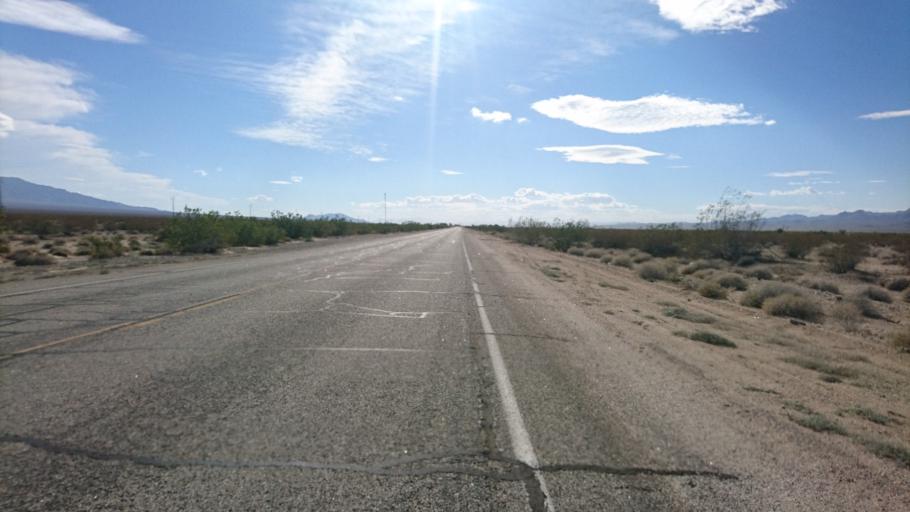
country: US
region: California
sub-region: San Bernardino County
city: Needles
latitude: 34.7449
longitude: -115.2356
